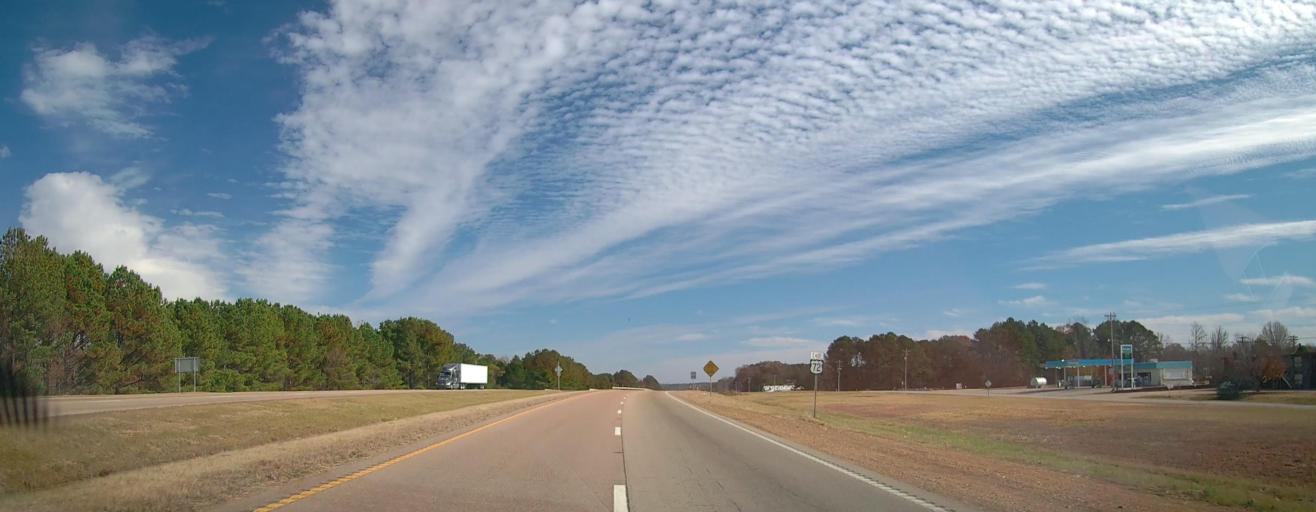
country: US
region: Mississippi
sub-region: Tippah County
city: Ripley
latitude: 34.9524
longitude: -88.9024
